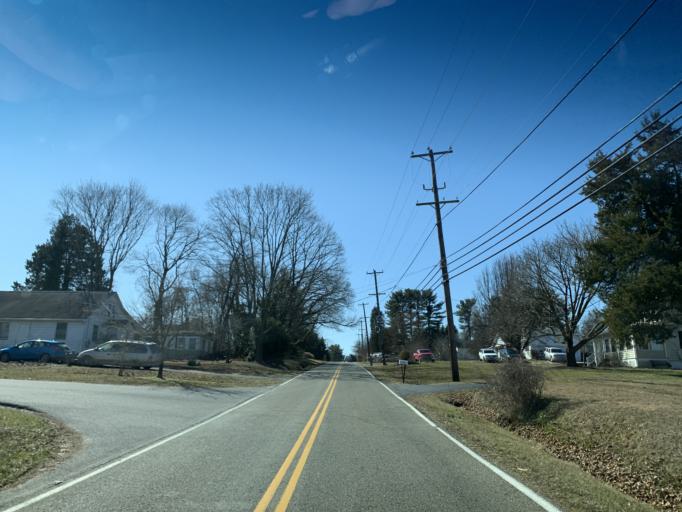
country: US
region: Maryland
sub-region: Cecil County
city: Elkton
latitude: 39.5214
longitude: -75.8196
